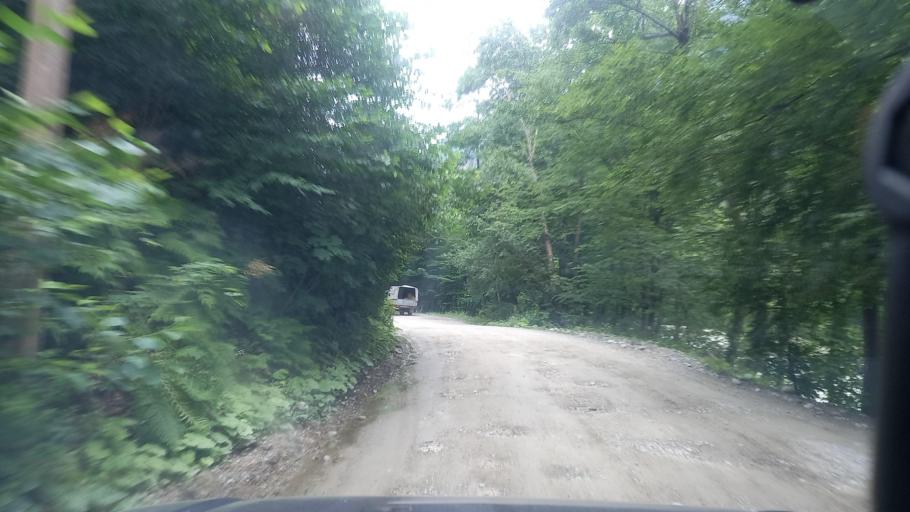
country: RU
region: Karachayevo-Cherkesiya
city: Kurdzhinovo
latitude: 43.8712
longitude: 40.9482
